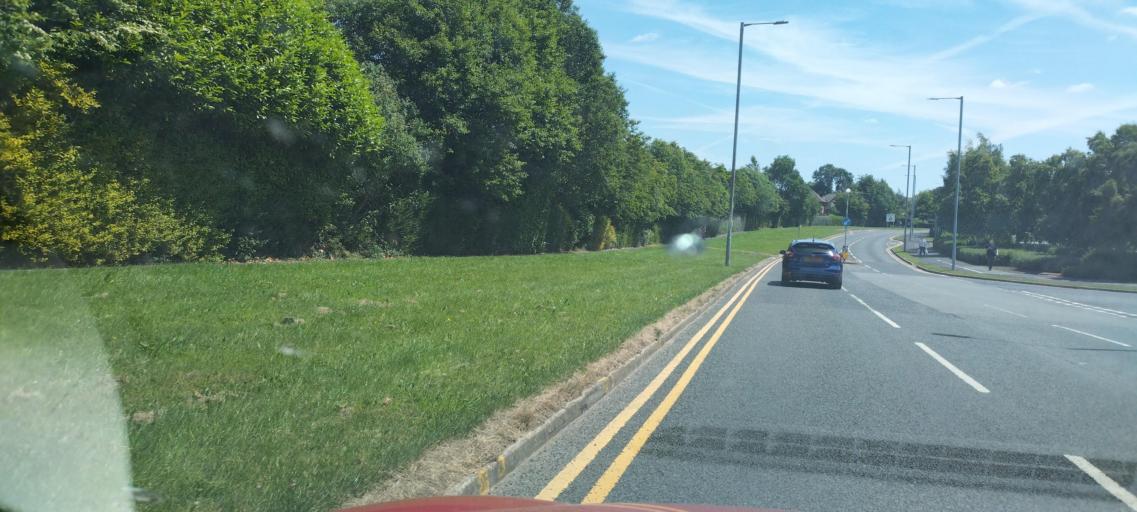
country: GB
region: England
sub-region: Borough of Bolton
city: Horwich
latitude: 53.5860
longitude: -2.5355
